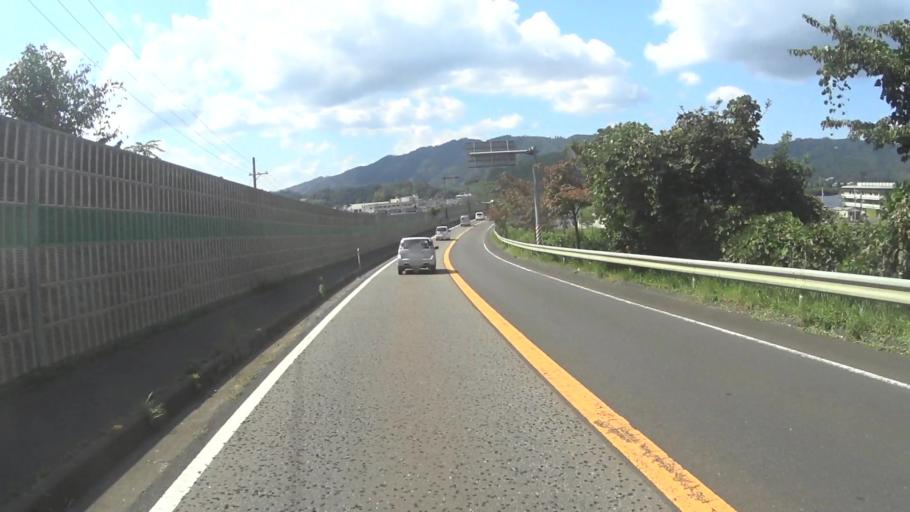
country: JP
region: Kyoto
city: Miyazu
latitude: 35.5516
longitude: 135.1614
